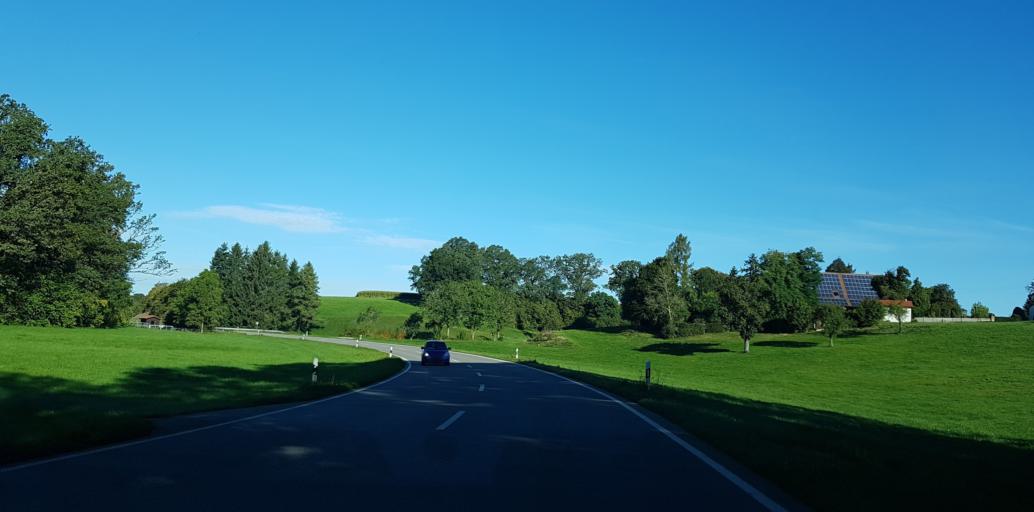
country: DE
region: Baden-Wuerttemberg
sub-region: Tuebingen Region
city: Eberhardzell
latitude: 47.9516
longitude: 9.8485
